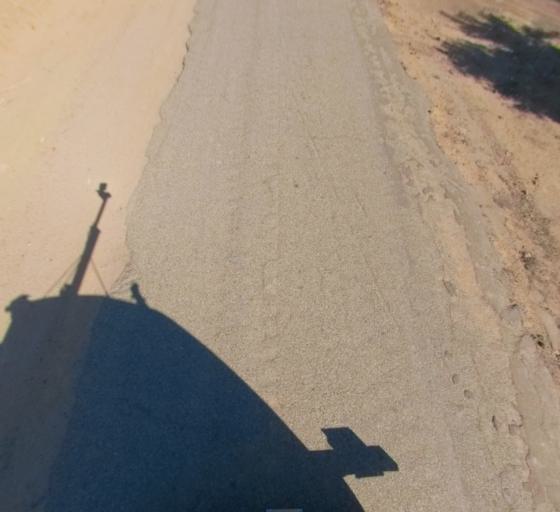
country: US
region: California
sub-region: Fresno County
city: Biola
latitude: 36.8518
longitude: -119.9082
